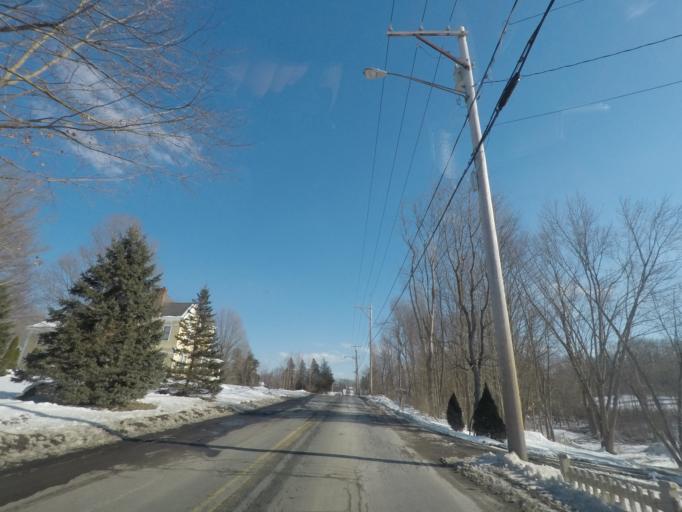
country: US
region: New York
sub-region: Saratoga County
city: Stillwater
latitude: 42.9070
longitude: -73.5126
